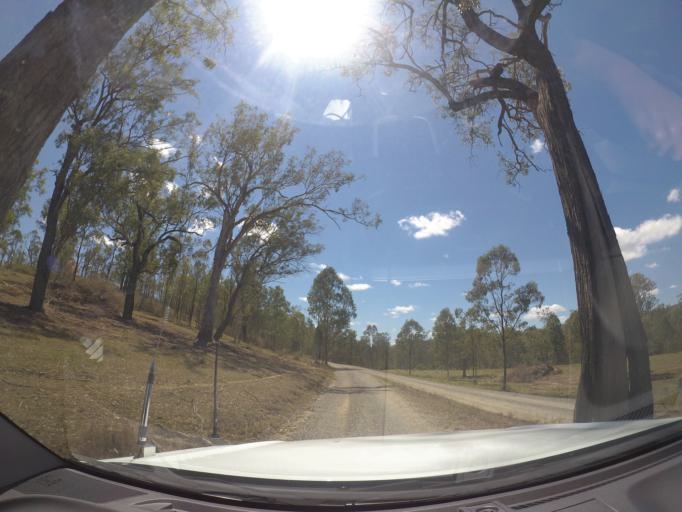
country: AU
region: Queensland
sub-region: Logan
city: Cedar Vale
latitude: -27.8667
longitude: 152.8465
